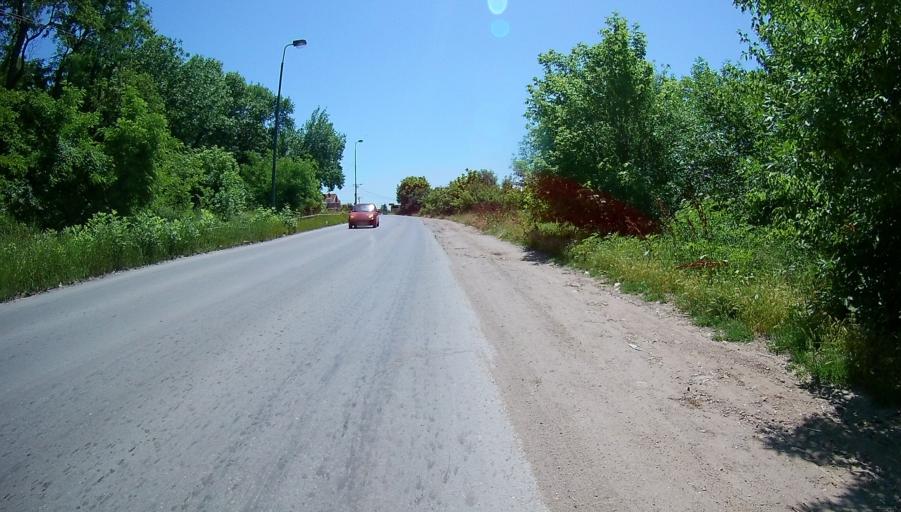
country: RS
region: Central Serbia
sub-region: Nisavski Okrug
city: Nis
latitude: 43.3059
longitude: 21.8672
